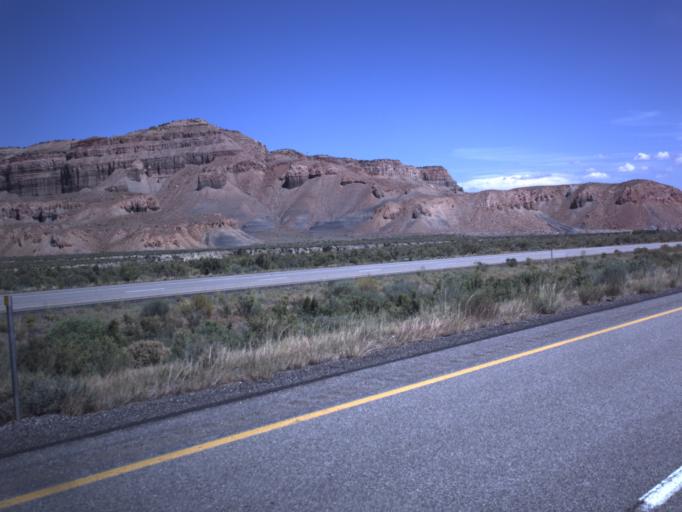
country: US
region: Utah
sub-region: Emery County
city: Ferron
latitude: 38.8099
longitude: -111.2473
